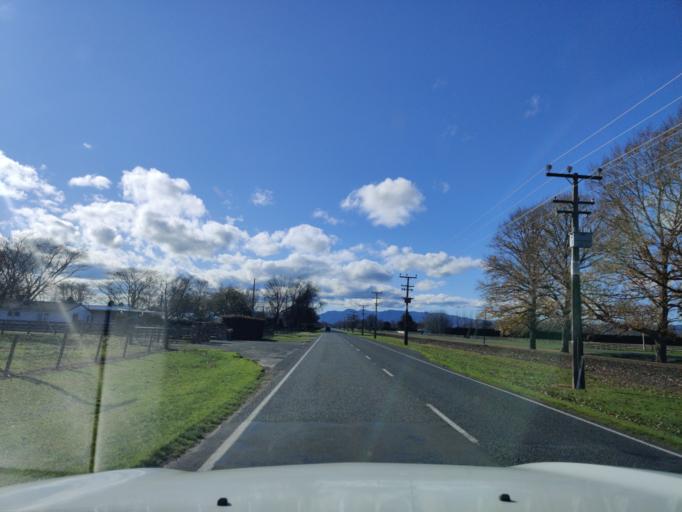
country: NZ
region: Waikato
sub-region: Matamata-Piako District
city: Matamata
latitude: -37.8411
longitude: 175.7632
